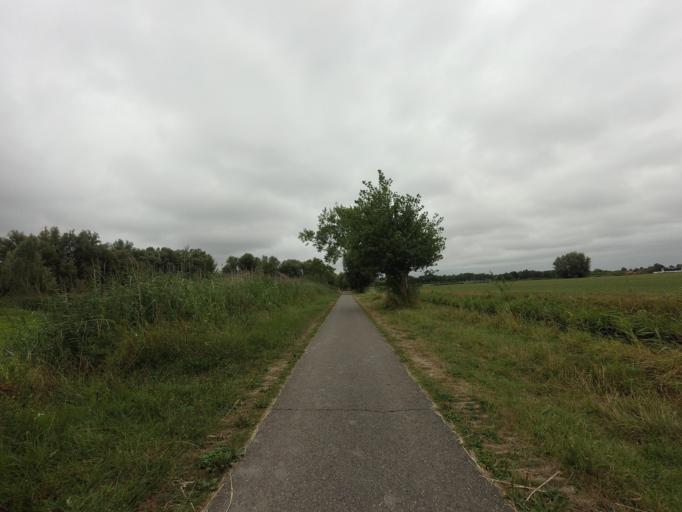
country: NL
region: Gelderland
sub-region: Gemeente Overbetuwe
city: Driel
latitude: 51.9583
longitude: 5.8314
